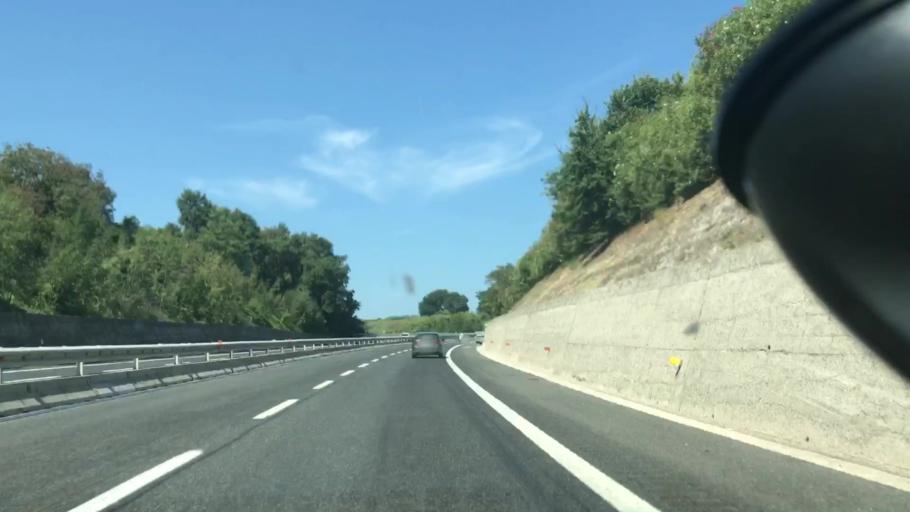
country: IT
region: Abruzzo
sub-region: Provincia di Chieti
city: Casalbordino-Miracoli
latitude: 42.1641
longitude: 14.6306
